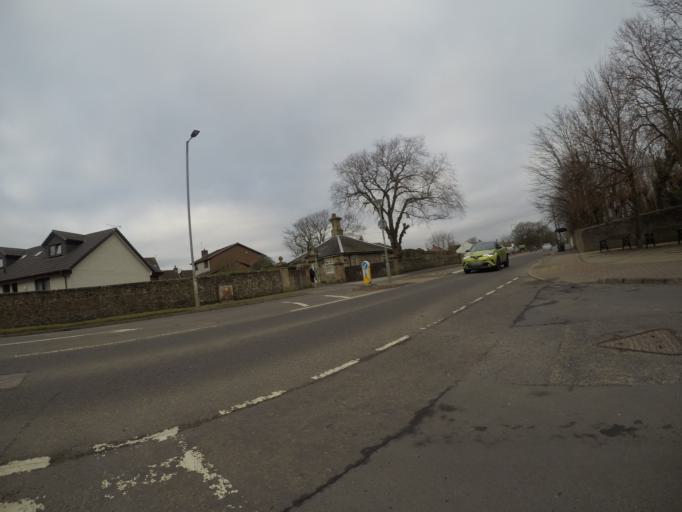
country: GB
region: Scotland
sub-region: North Ayrshire
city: Irvine
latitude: 55.6237
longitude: -4.6722
